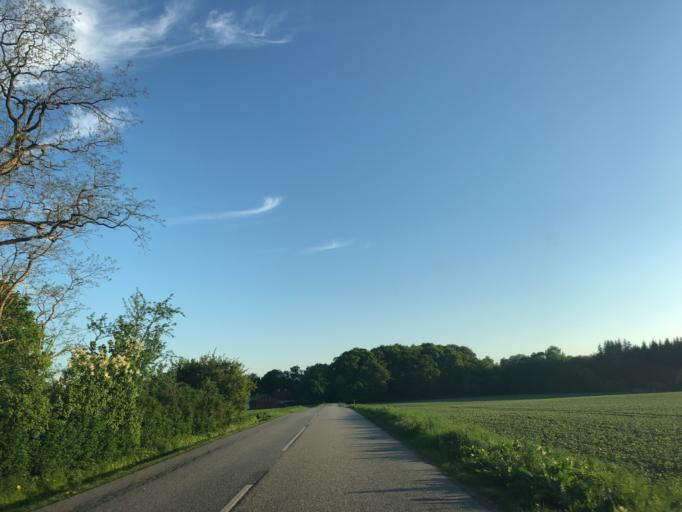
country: DK
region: Zealand
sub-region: Koge Kommune
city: Borup
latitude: 55.4383
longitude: 11.9458
